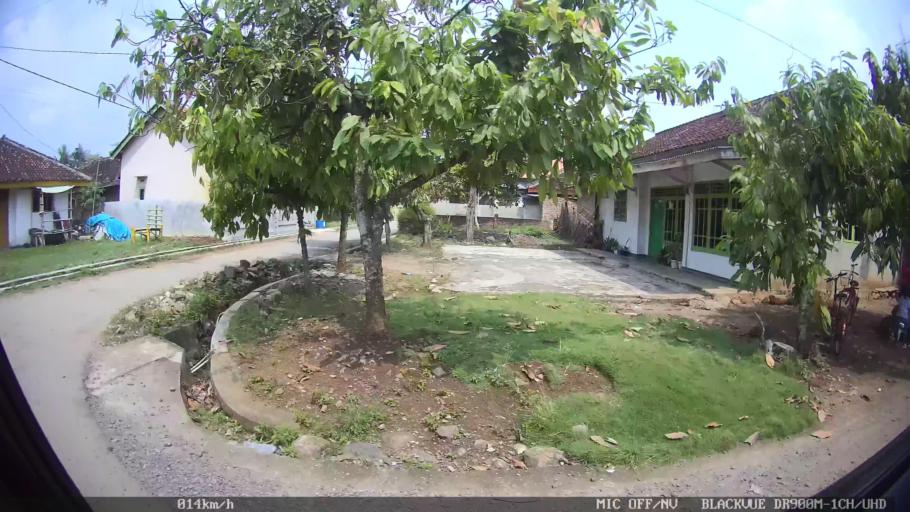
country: ID
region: Lampung
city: Gadingrejo
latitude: -5.3685
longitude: 105.0576
